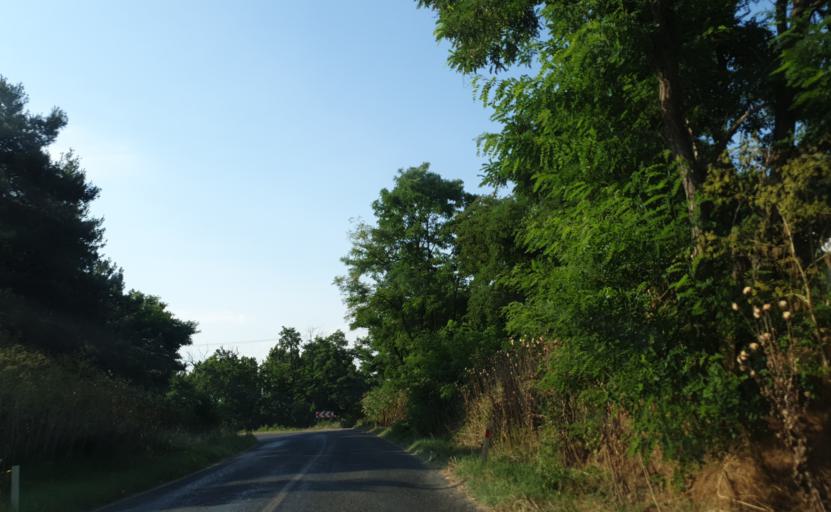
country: TR
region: Tekirdag
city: Muratli
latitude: 41.1930
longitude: 27.4760
